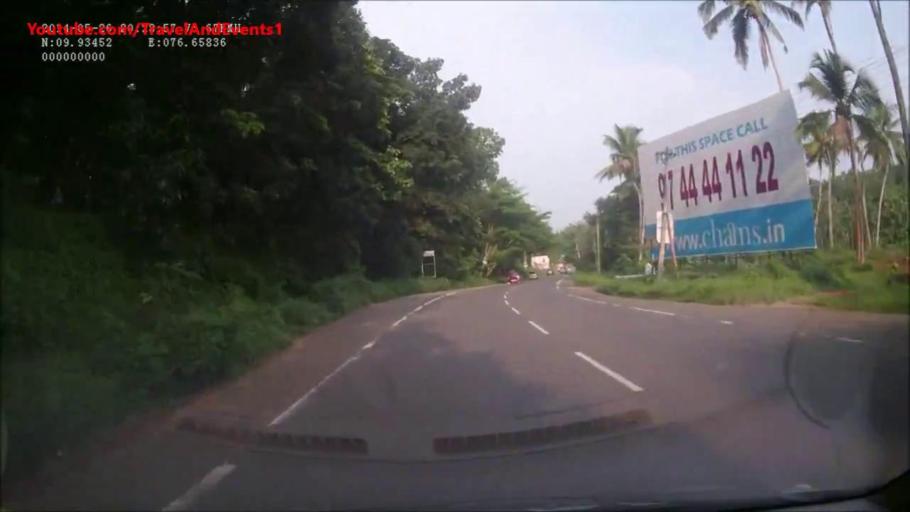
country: IN
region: Kerala
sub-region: Ernakulam
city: Muvattupula
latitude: 9.9318
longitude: 76.6640
